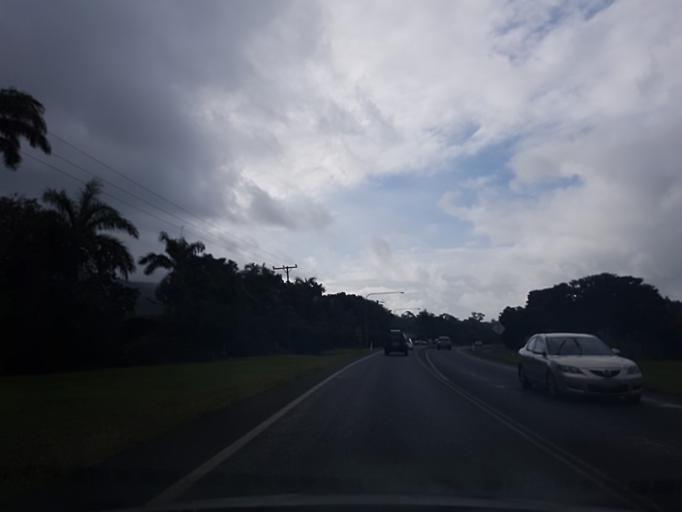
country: AU
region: Queensland
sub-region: Cairns
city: Trinity Beach
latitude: -16.7844
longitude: 145.6734
